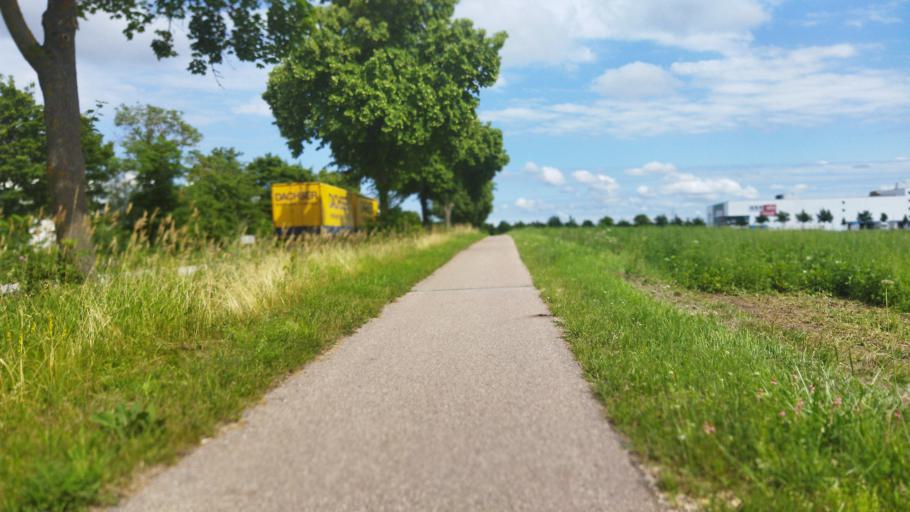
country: DE
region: Bavaria
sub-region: Upper Palatinate
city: Tegernheim
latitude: 49.0071
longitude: 12.1727
